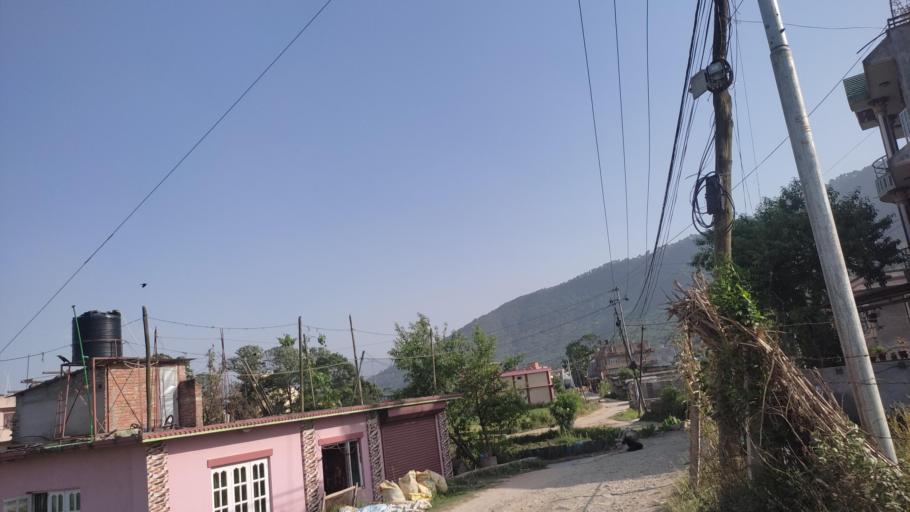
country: NP
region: Central Region
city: Kirtipur
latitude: 27.6540
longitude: 85.2797
